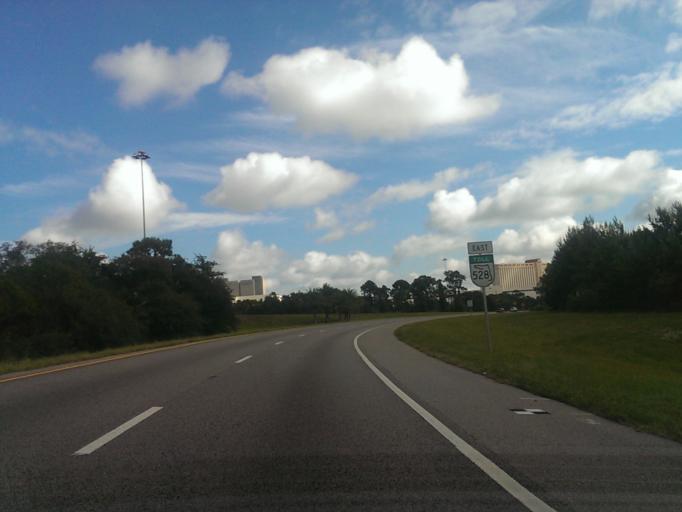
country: US
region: Florida
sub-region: Orange County
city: Williamsburg
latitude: 28.4188
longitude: -81.4733
